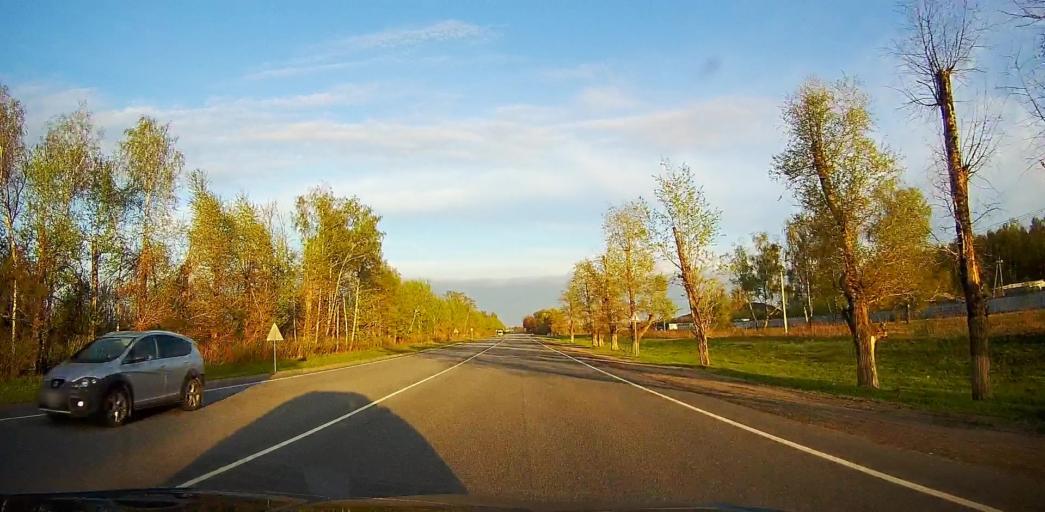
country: RU
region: Moskovskaya
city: Troitskoye
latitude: 55.2154
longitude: 38.5935
